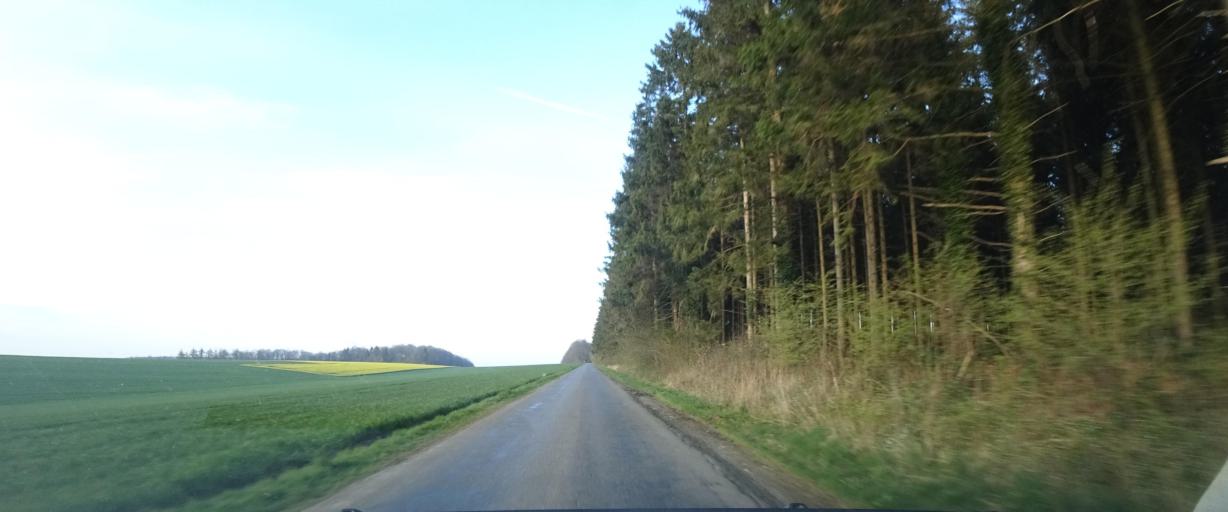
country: BE
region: Wallonia
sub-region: Province de Namur
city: Hamois
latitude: 50.3265
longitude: 5.2106
